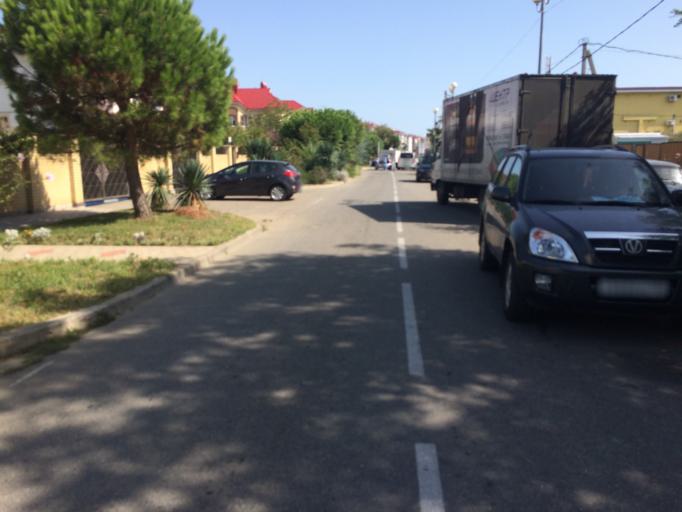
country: RU
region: Krasnodarskiy
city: Adler
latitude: 43.3979
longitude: 39.9708
